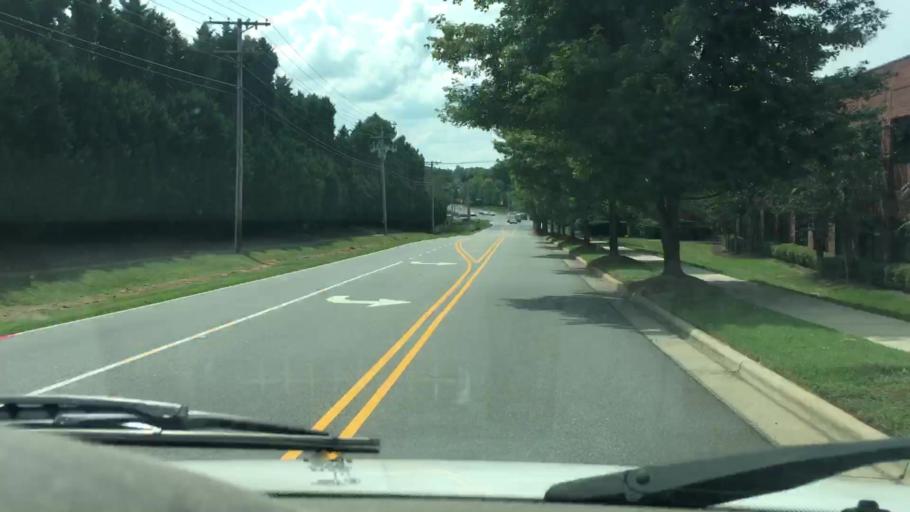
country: US
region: North Carolina
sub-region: Mecklenburg County
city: Cornelius
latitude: 35.4460
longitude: -80.8734
